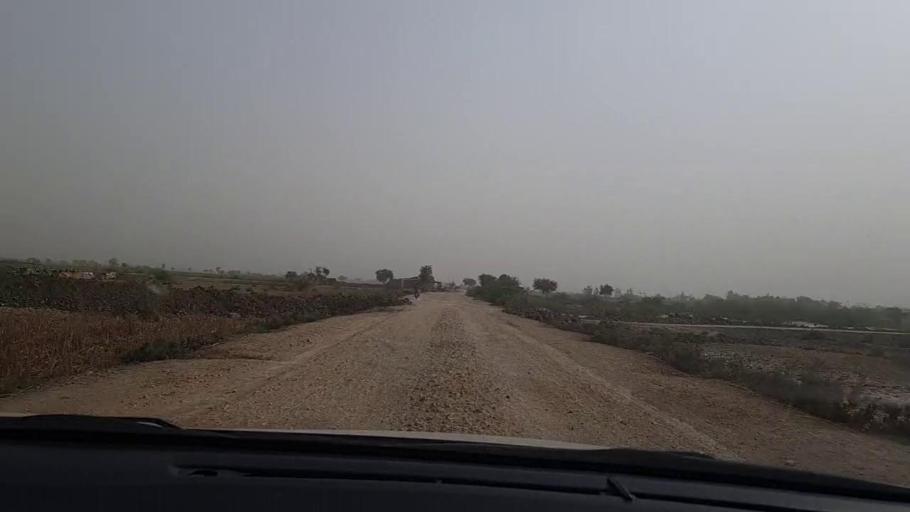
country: PK
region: Sindh
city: Pithoro
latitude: 25.4114
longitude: 69.3174
